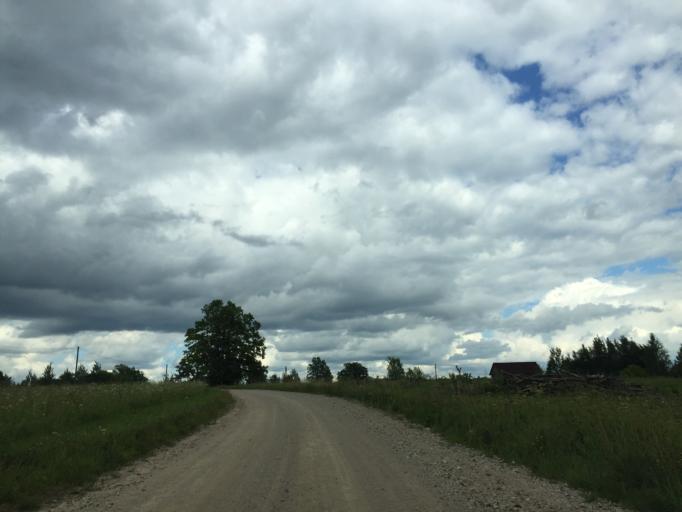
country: LV
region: Malpils
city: Malpils
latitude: 56.9155
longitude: 24.9984
